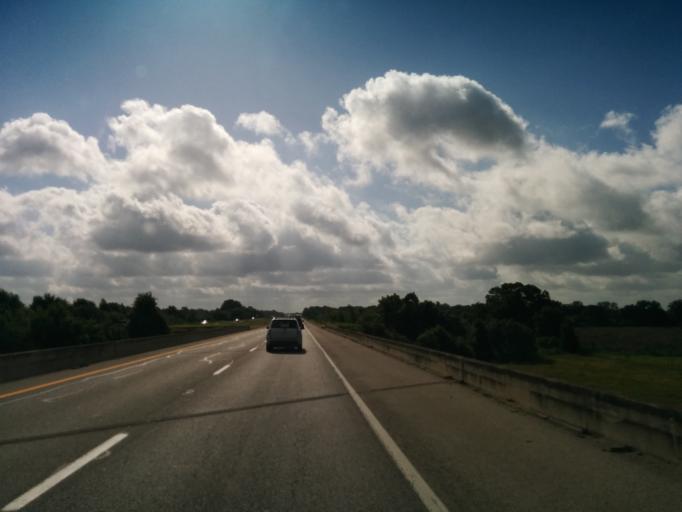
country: US
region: Texas
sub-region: Caldwell County
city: Luling
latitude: 29.6496
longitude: -97.6407
